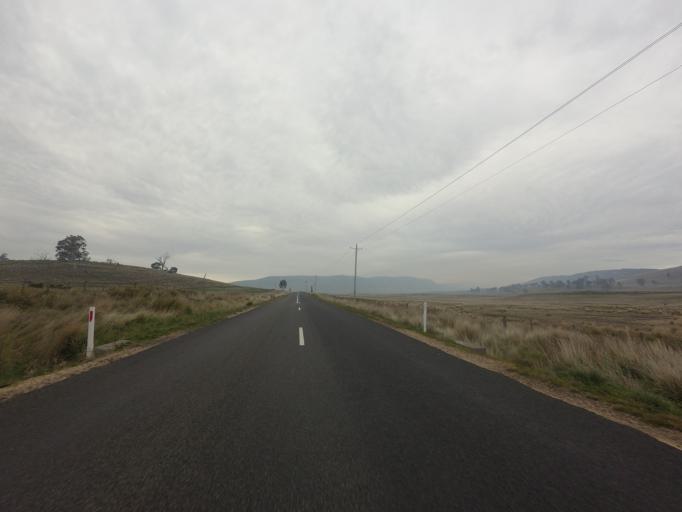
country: AU
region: Tasmania
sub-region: Derwent Valley
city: New Norfolk
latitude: -42.4448
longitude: 146.9697
